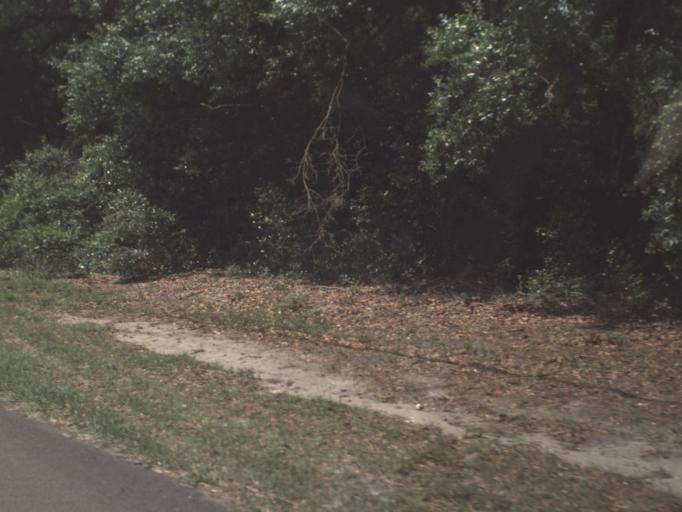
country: US
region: Florida
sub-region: Lake County
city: Umatilla
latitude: 28.9733
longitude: -81.6461
